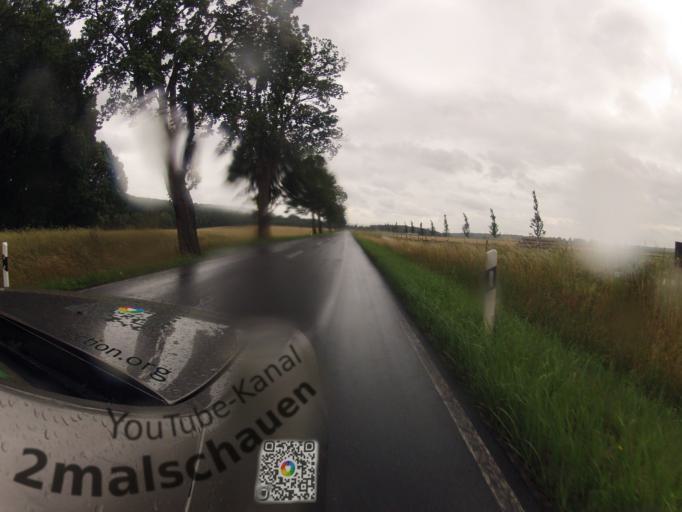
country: DE
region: Mecklenburg-Vorpommern
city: Seebad Heringsdorf
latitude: 53.9084
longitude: 14.1496
